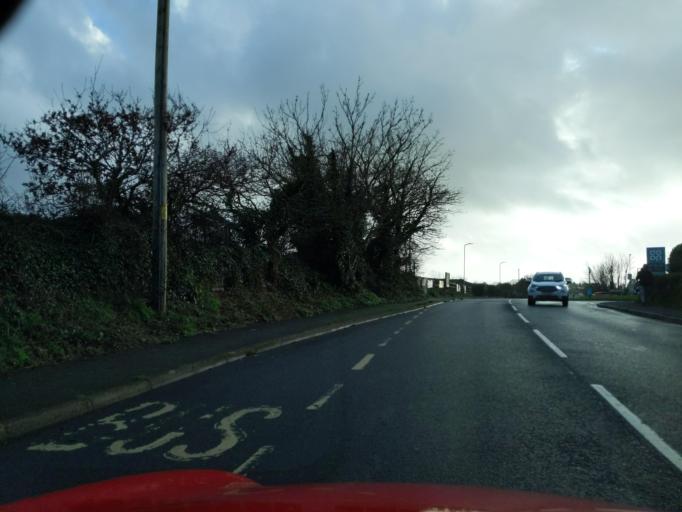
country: GB
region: England
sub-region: Plymouth
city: Plymstock
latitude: 50.3522
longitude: -4.0751
